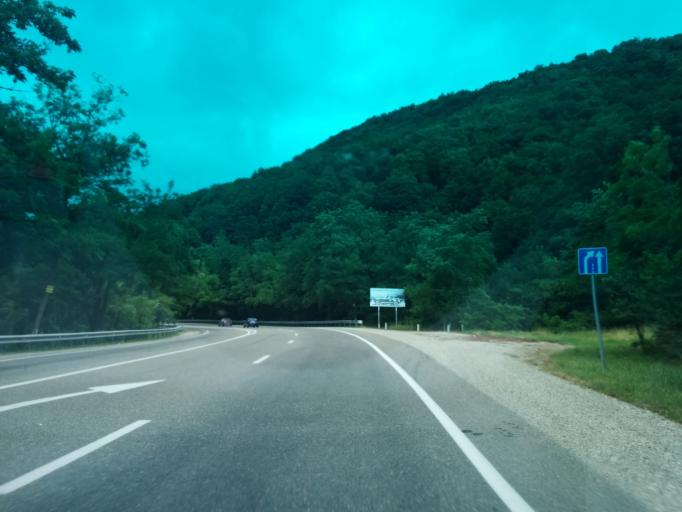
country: RU
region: Krasnodarskiy
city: Nebug
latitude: 44.1765
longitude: 38.9541
